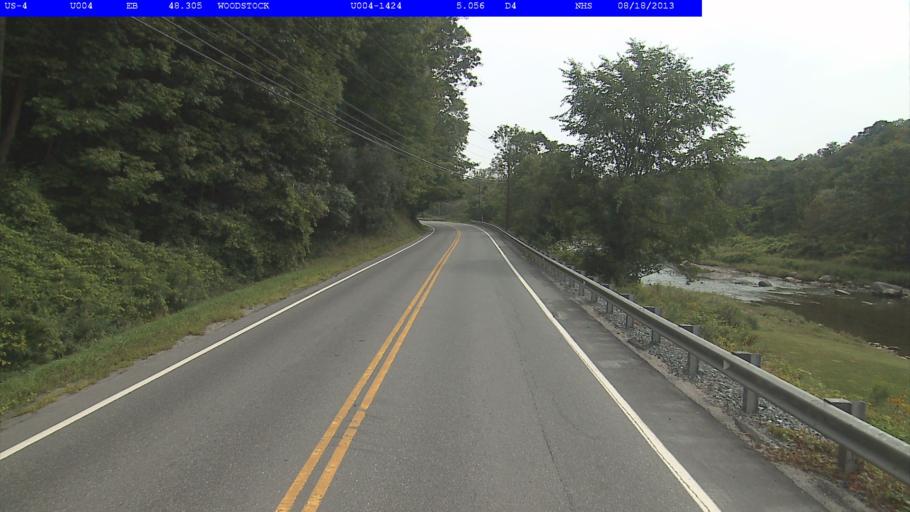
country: US
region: Vermont
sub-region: Windsor County
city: Woodstock
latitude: 43.6176
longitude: -72.5391
